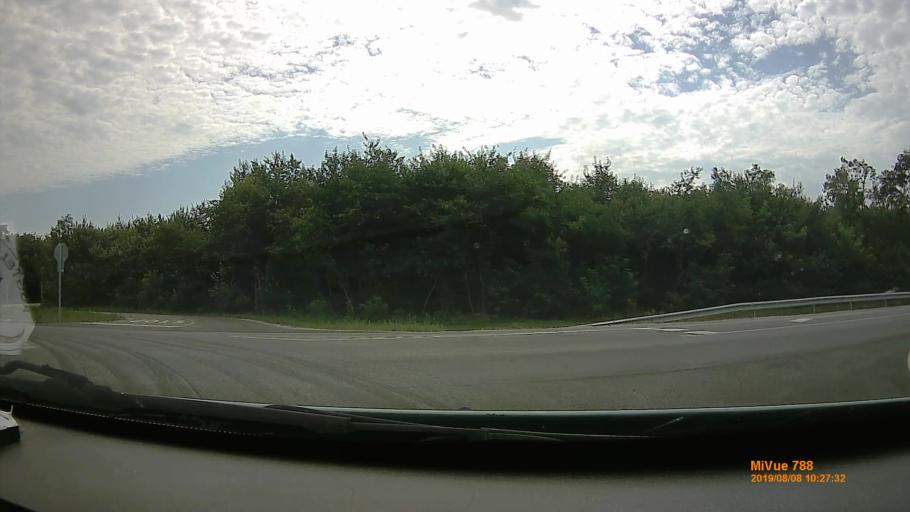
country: HU
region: Hajdu-Bihar
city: Hajdusamson
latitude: 47.6265
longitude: 21.7895
